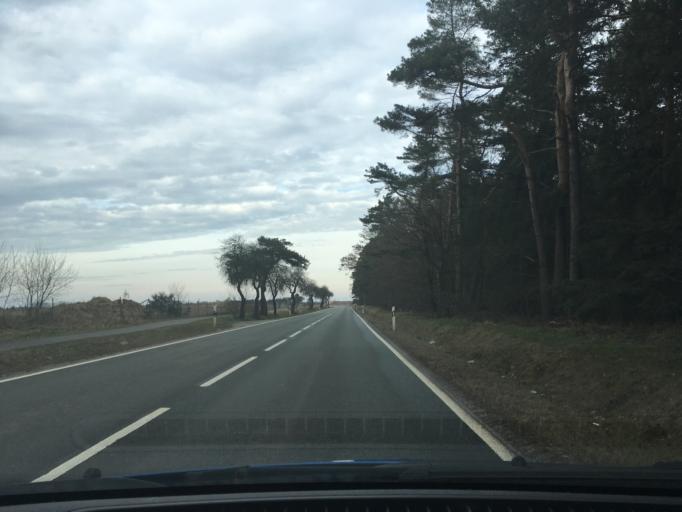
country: DE
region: Mecklenburg-Vorpommern
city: Zarrentin
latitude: 53.5148
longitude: 10.8958
